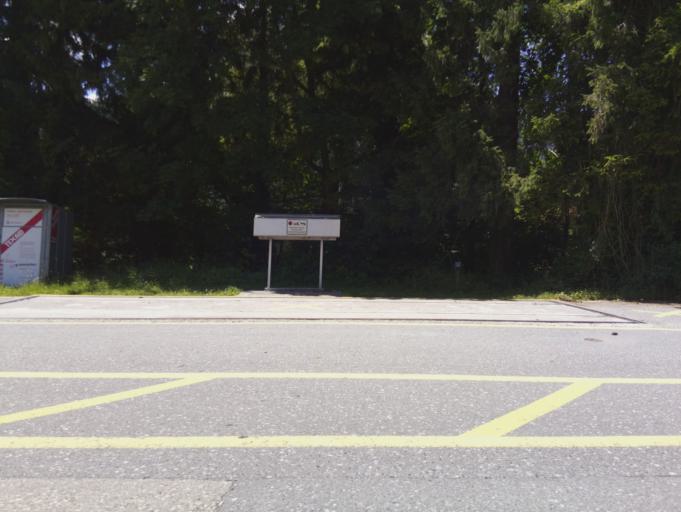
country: CH
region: Glarus
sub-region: Glarus
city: Nafels
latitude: 47.1008
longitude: 9.0706
